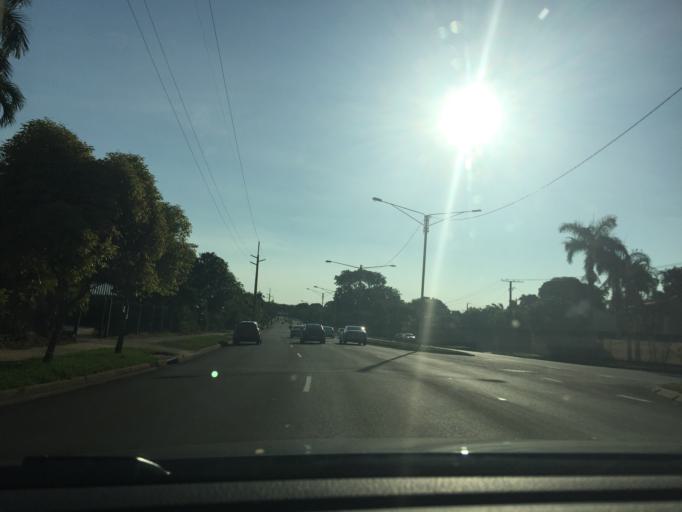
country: AU
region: Northern Territory
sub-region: Darwin
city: Nightcliff
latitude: -12.3837
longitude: 130.8708
